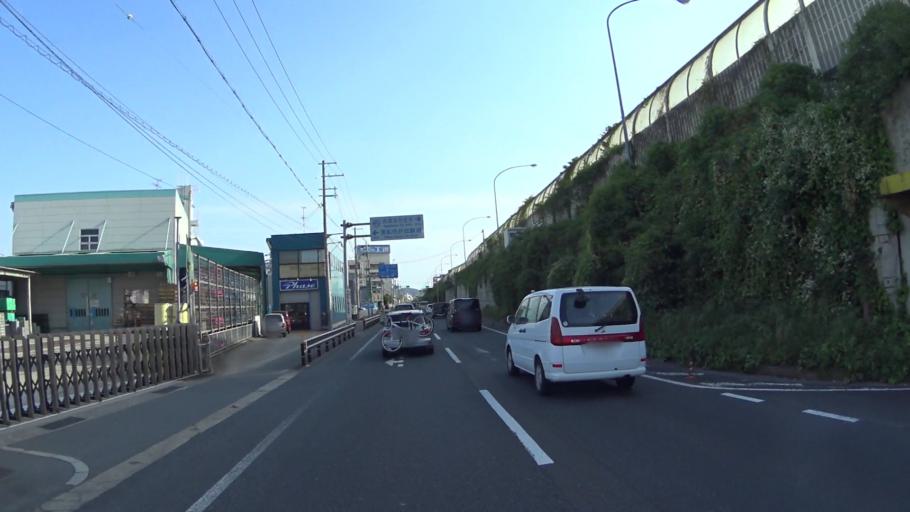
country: JP
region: Kyoto
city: Muko
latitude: 34.9234
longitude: 135.7149
